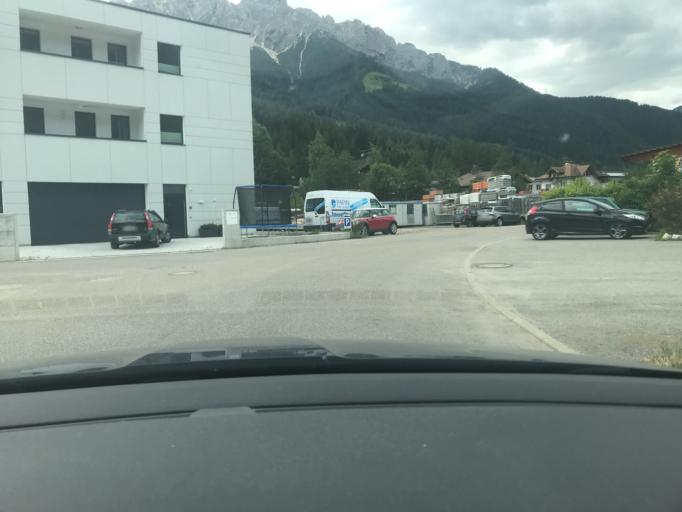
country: IT
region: Trentino-Alto Adige
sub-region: Bolzano
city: San Candido
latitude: 46.7306
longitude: 12.2702
